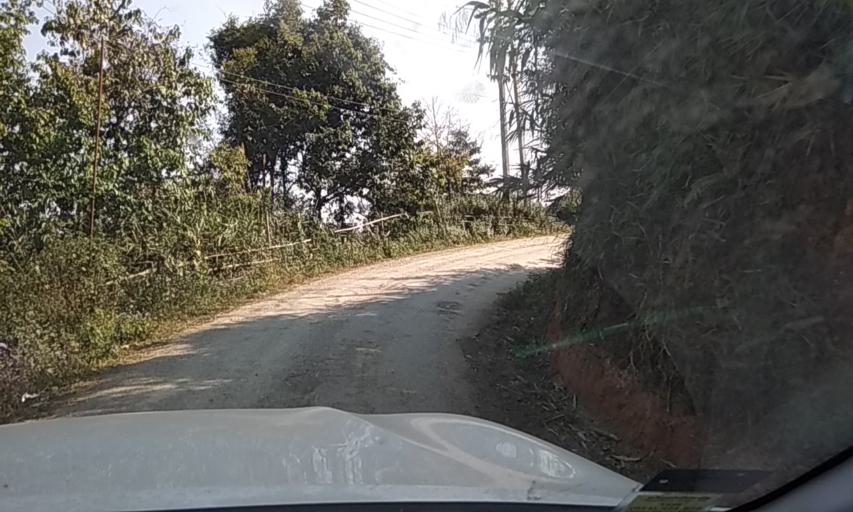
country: LA
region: Phongsali
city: Phongsali
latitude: 21.6587
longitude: 102.0913
